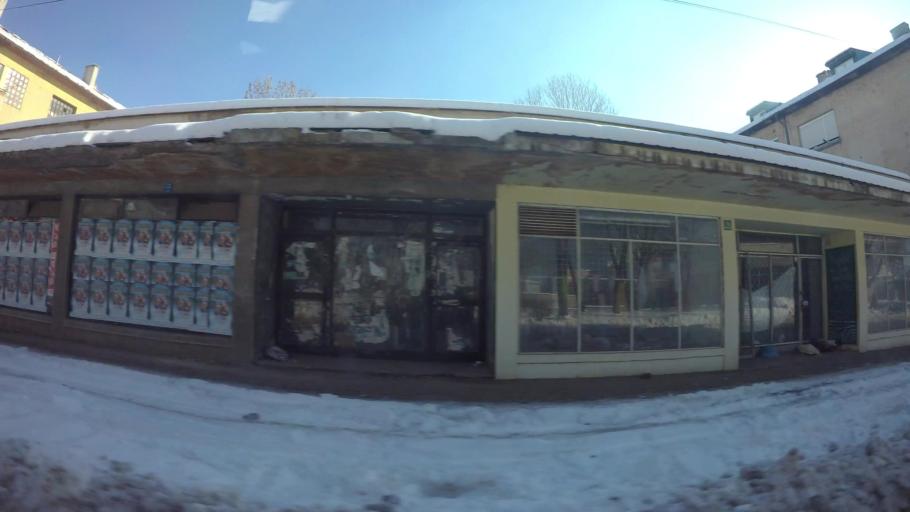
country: BA
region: Federation of Bosnia and Herzegovina
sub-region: Kanton Sarajevo
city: Sarajevo
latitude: 43.7979
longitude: 18.3145
